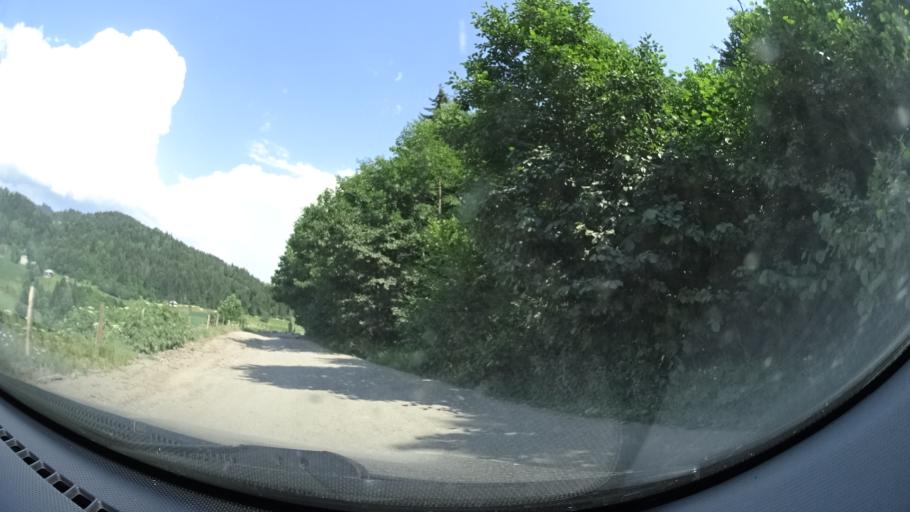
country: GE
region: Ajaria
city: Dioknisi
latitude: 41.6516
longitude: 42.4646
